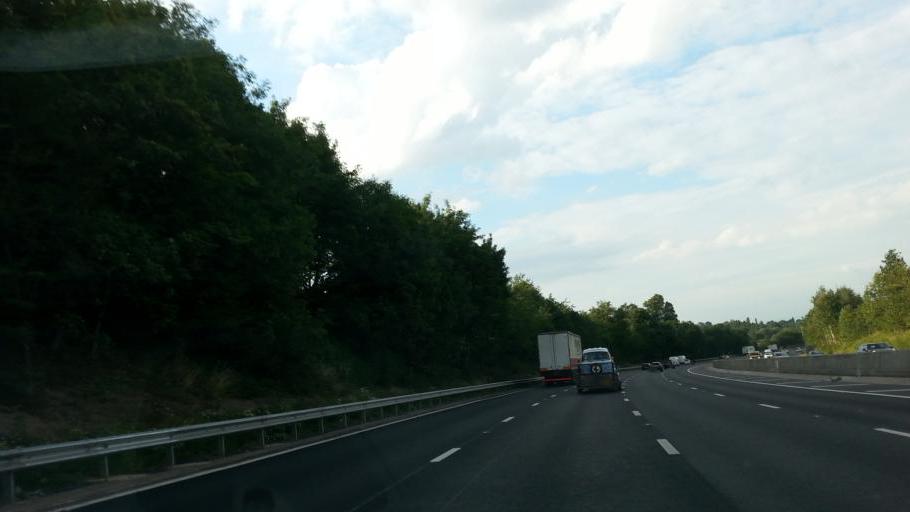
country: GB
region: England
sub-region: Worcestershire
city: Droitwich
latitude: 52.2629
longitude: -2.1373
